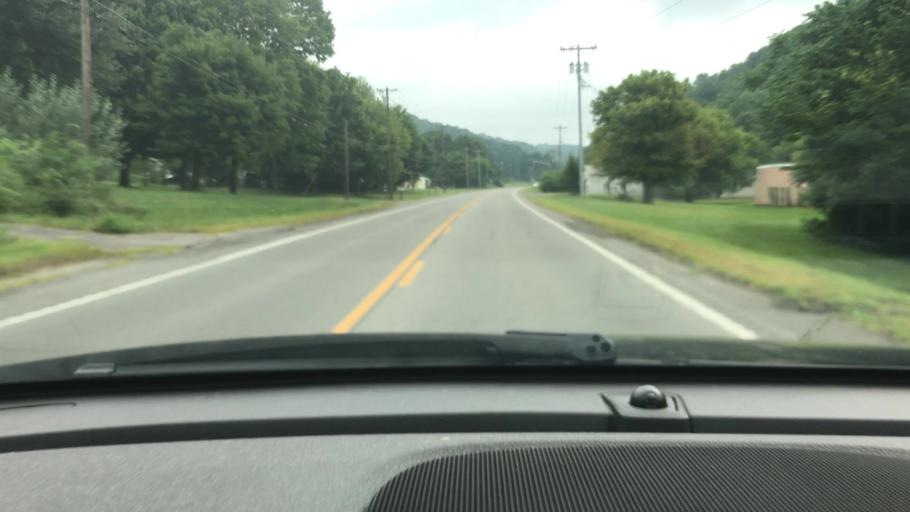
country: US
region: Tennessee
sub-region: Sumner County
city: Millersville
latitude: 36.3824
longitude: -86.7020
